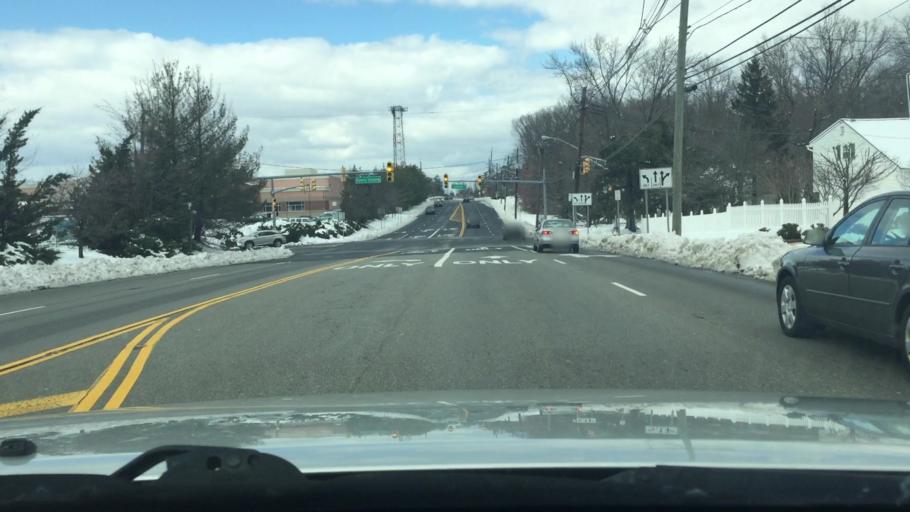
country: US
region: New Jersey
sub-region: Middlesex County
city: East Brunswick
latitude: 40.4433
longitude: -74.4235
